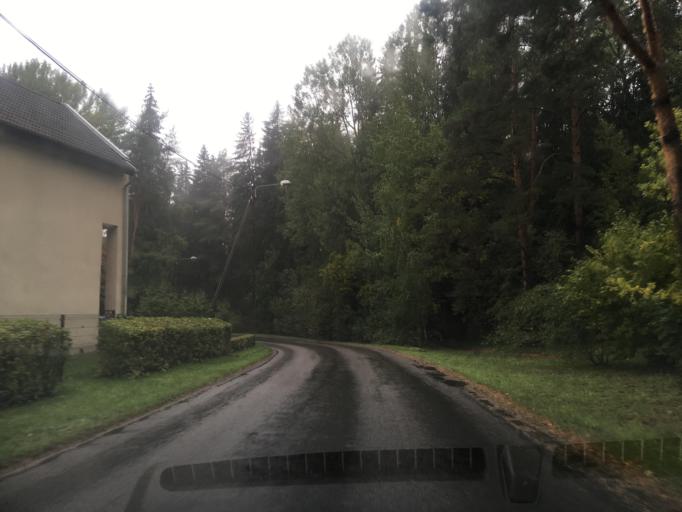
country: EE
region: Tartu
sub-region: Tartu linn
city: Tartu
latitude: 58.3599
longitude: 26.7873
